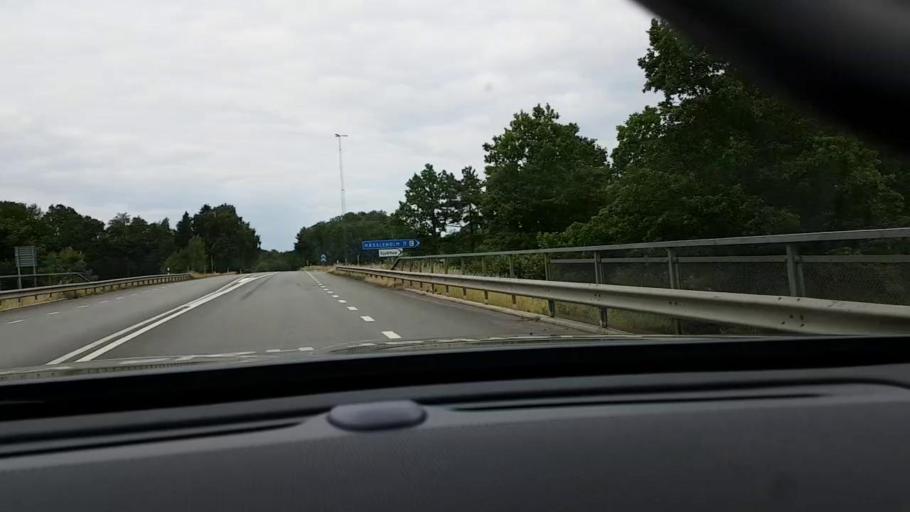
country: SE
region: Skane
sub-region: Hassleholms Kommun
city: Hassleholm
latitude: 56.1402
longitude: 13.8032
